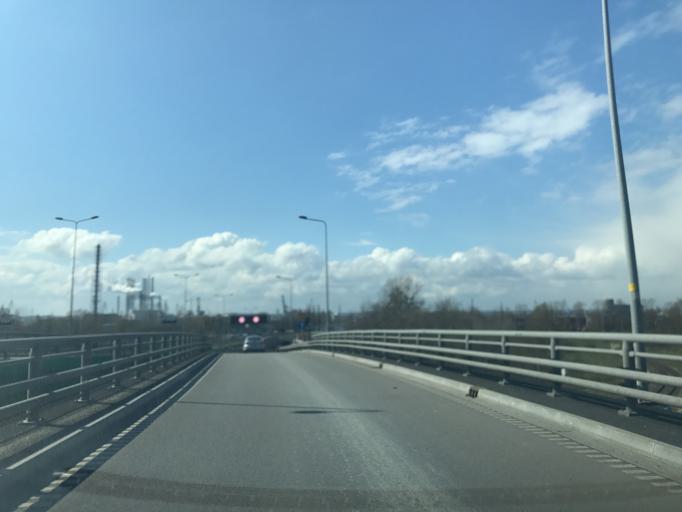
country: PL
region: Pomeranian Voivodeship
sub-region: Gdansk
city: Gdansk
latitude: 54.3790
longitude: 18.6772
